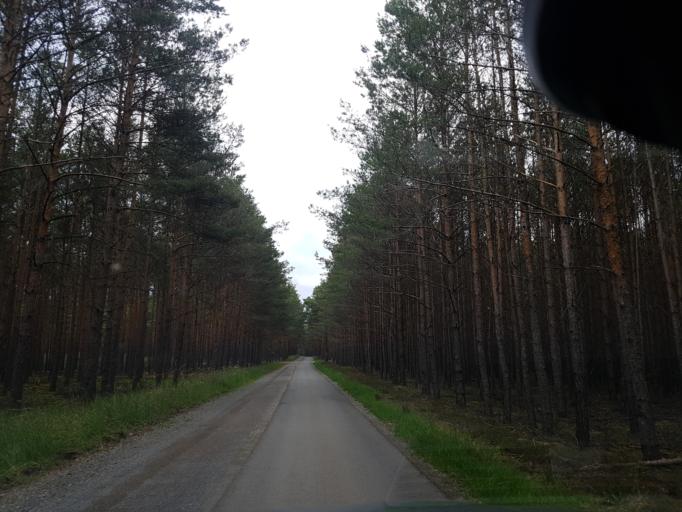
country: DE
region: Brandenburg
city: Crinitz
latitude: 51.6832
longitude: 13.7789
